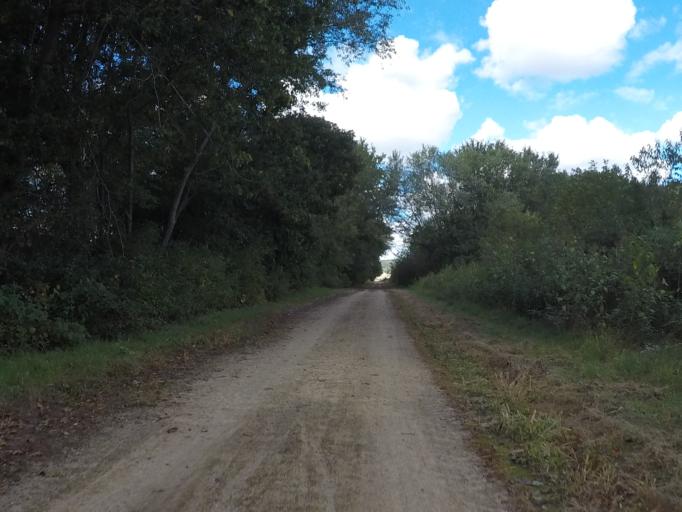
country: US
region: Wisconsin
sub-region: Richland County
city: Richland Center
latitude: 43.3068
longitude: -90.3424
